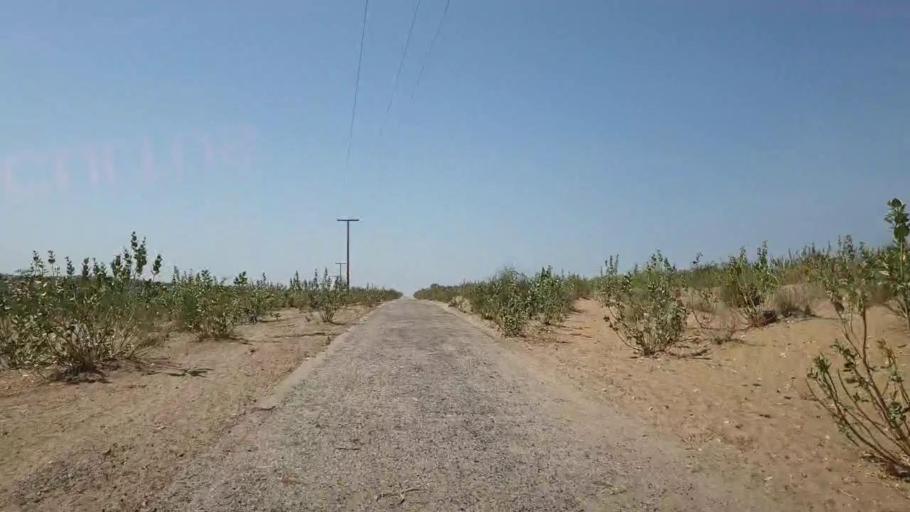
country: PK
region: Sindh
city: Umarkot
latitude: 25.1629
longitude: 69.9599
